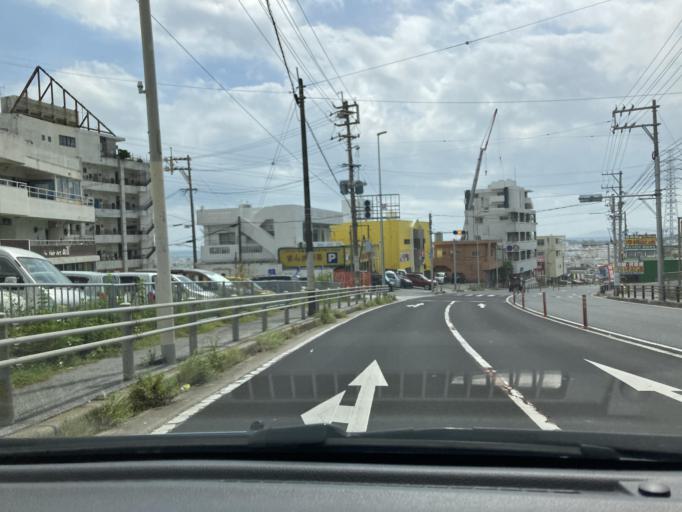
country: JP
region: Okinawa
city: Okinawa
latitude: 26.3313
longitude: 127.8223
